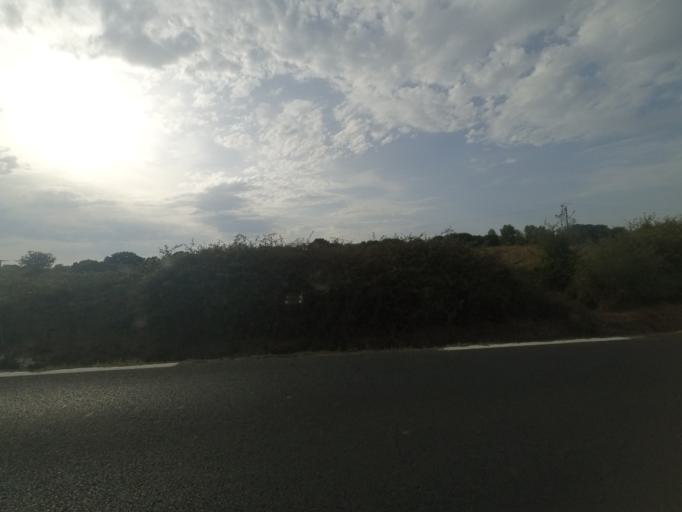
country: FR
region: Languedoc-Roussillon
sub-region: Departement de l'Herault
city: Restinclieres
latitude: 43.7133
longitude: 4.0295
